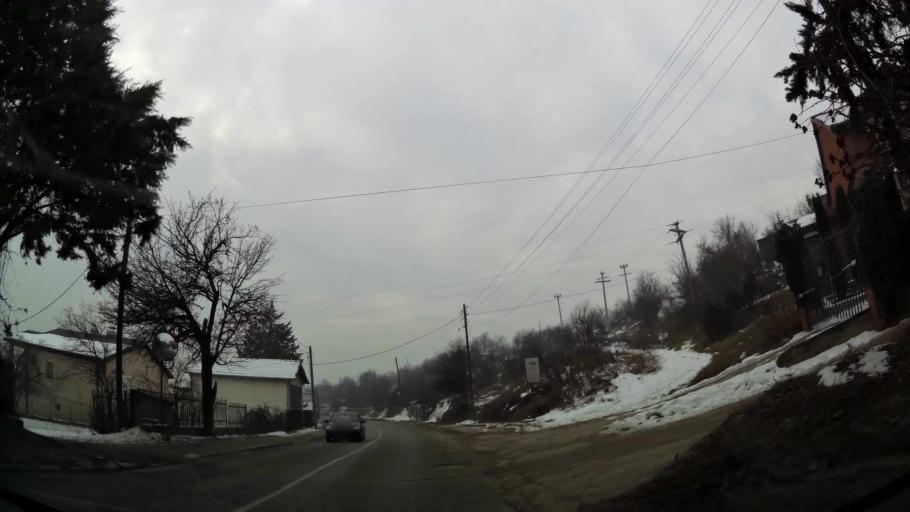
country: MK
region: Saraj
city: Saraj
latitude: 42.0348
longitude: 21.3484
